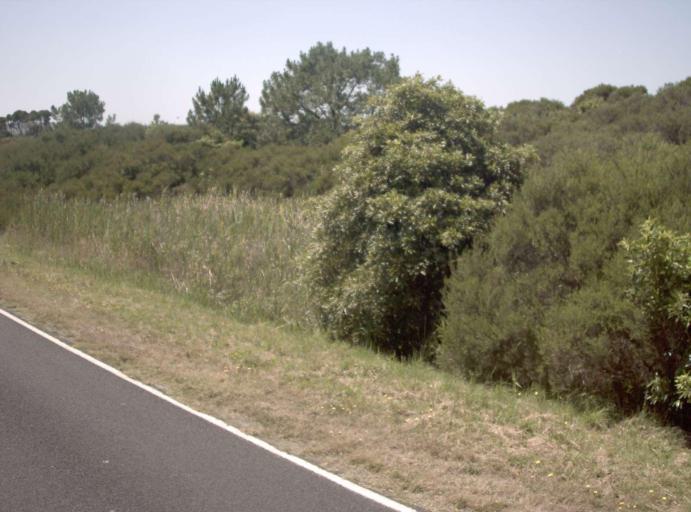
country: AU
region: Victoria
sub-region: Bass Coast
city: North Wonthaggi
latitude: -38.6270
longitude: 145.8113
